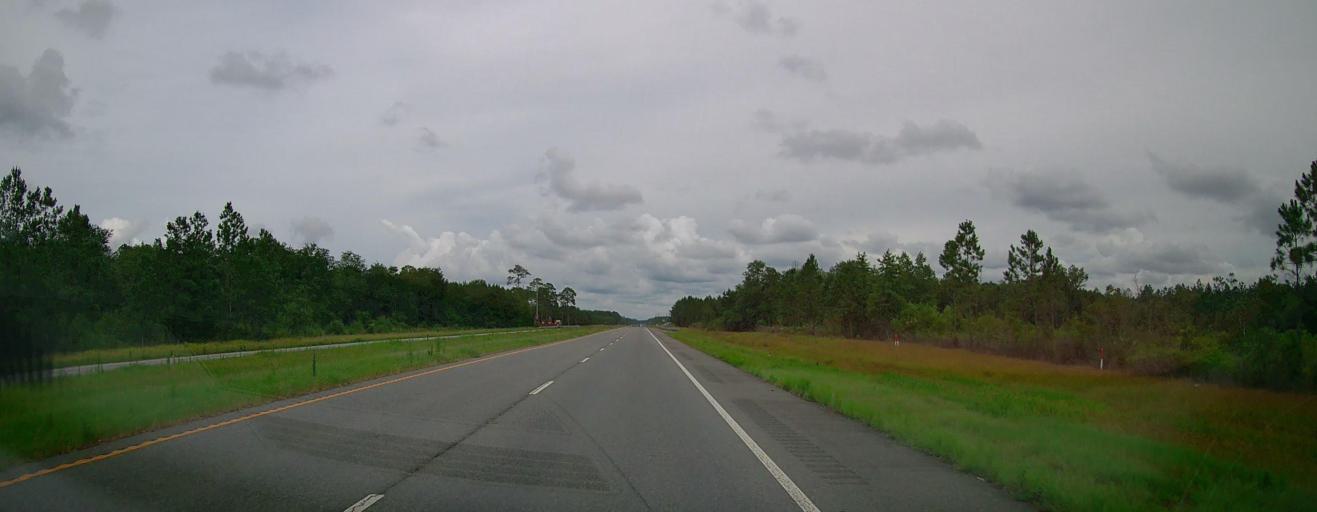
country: US
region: Georgia
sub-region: Appling County
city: Baxley
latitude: 31.7396
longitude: -82.2371
